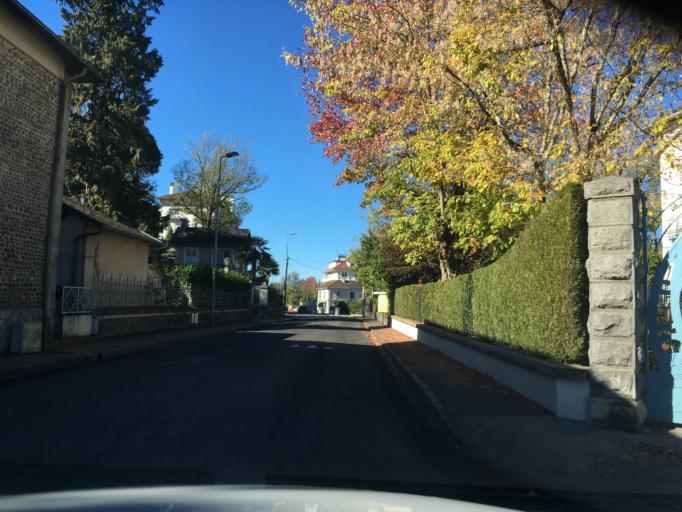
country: FR
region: Aquitaine
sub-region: Departement des Pyrenees-Atlantiques
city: Bizanos
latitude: 43.2991
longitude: -0.3469
